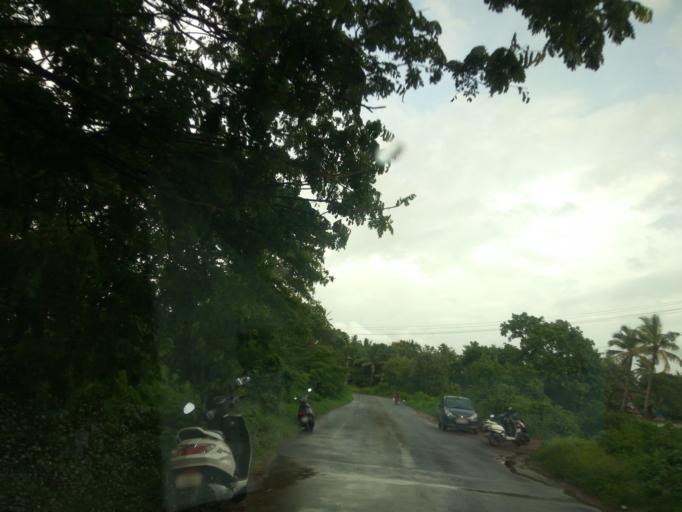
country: IN
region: Goa
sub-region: North Goa
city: Goa Velha
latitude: 15.4421
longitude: 73.8676
